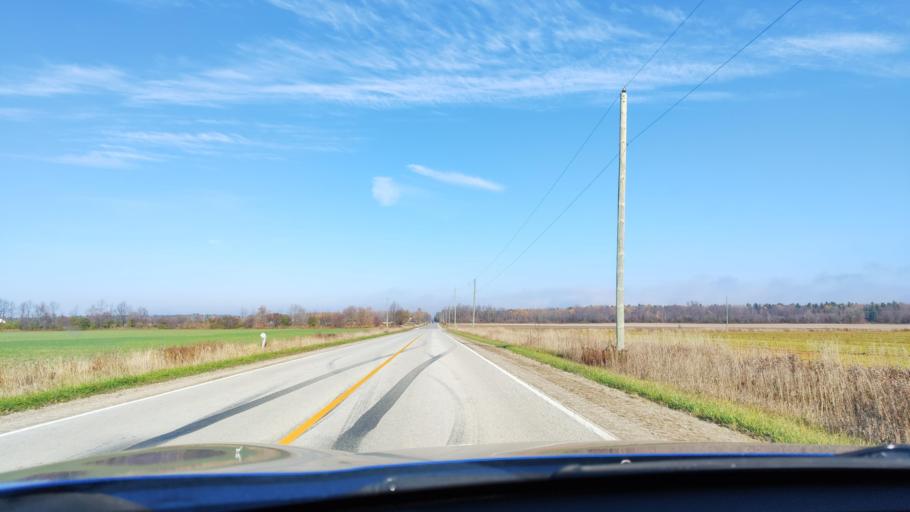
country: CA
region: Ontario
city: Wasaga Beach
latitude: 44.3957
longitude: -80.0568
